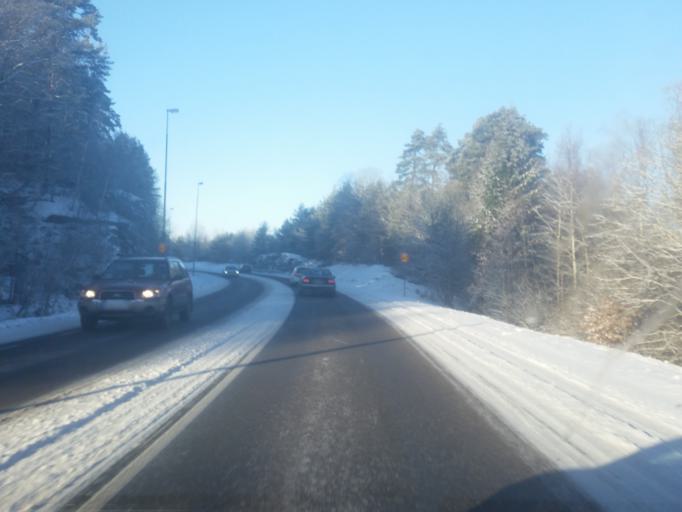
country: SE
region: Vaestra Goetaland
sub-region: Partille Kommun
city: Furulund
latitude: 57.7212
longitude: 12.1377
